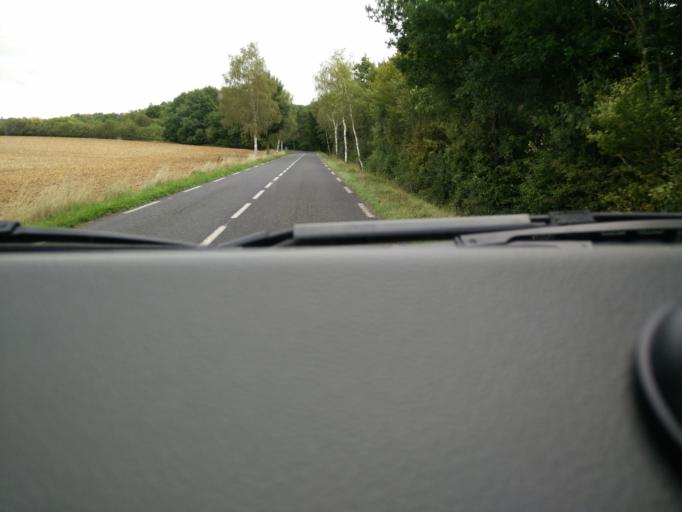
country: FR
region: Lorraine
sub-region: Departement de Meurthe-et-Moselle
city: Montauville
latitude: 48.9417
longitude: 5.8868
